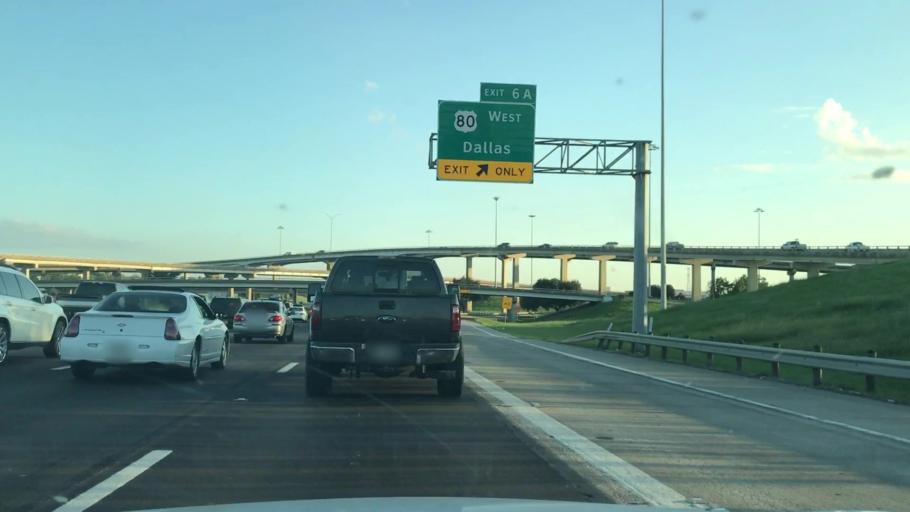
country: US
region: Texas
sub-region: Dallas County
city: Mesquite
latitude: 32.7955
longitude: -96.6257
